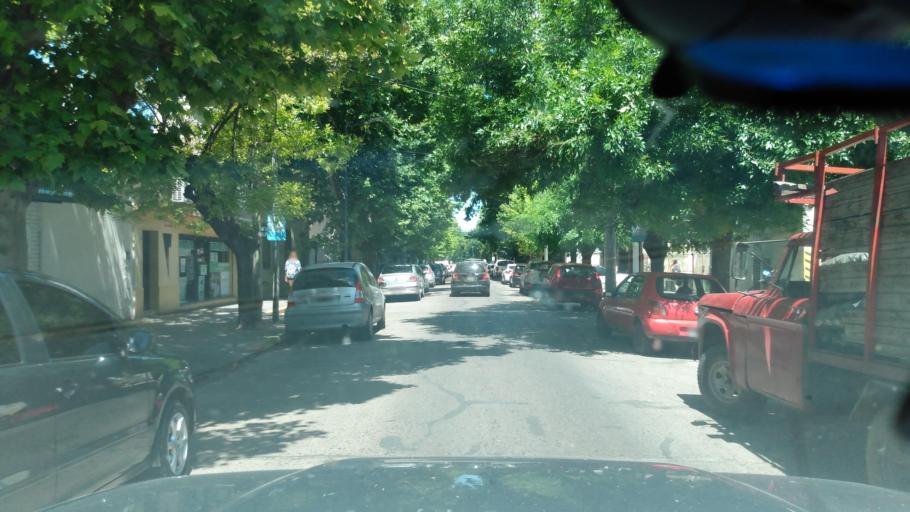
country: AR
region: Buenos Aires
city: Hurlingham
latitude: -34.5417
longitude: -58.7093
